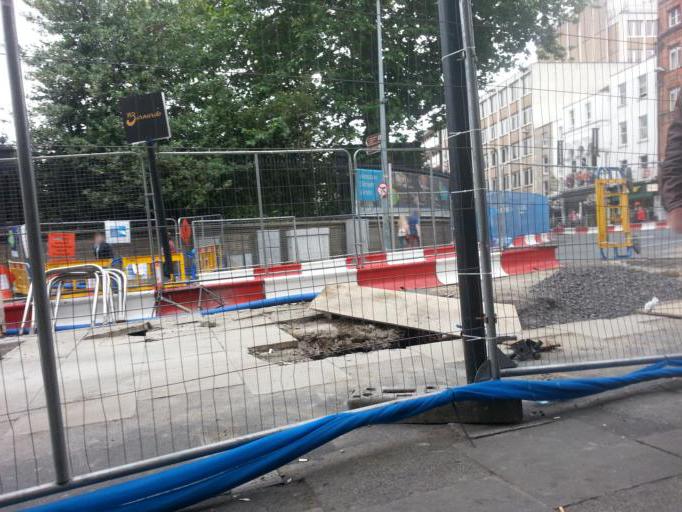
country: IE
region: Leinster
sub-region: Dublin City
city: Dublin
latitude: 53.3434
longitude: -6.2594
